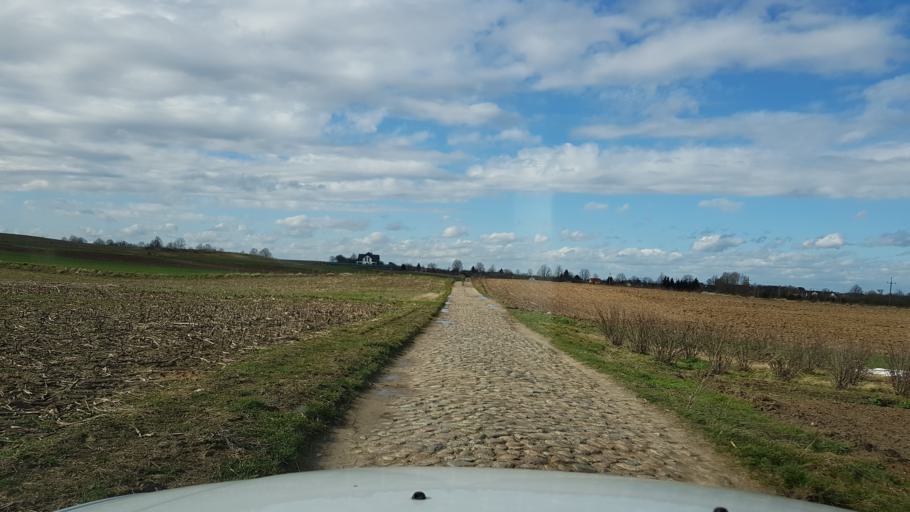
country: PL
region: West Pomeranian Voivodeship
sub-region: Powiat mysliborski
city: Barlinek
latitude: 52.9747
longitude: 15.1800
